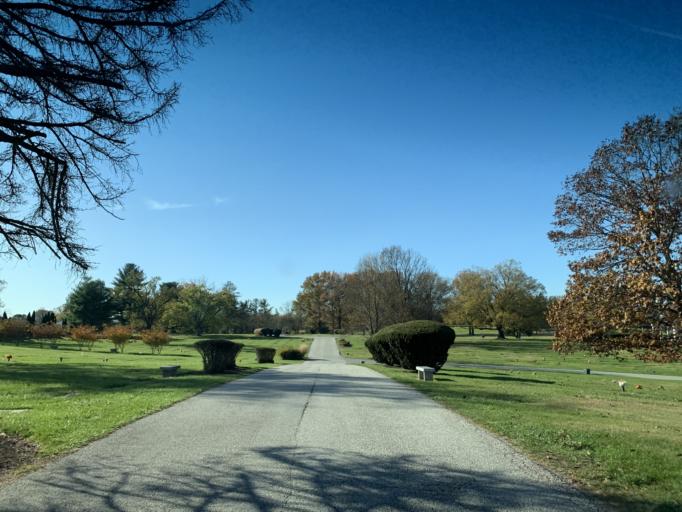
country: US
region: Maryland
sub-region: Baltimore County
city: Timonium
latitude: 39.4563
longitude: -76.6186
